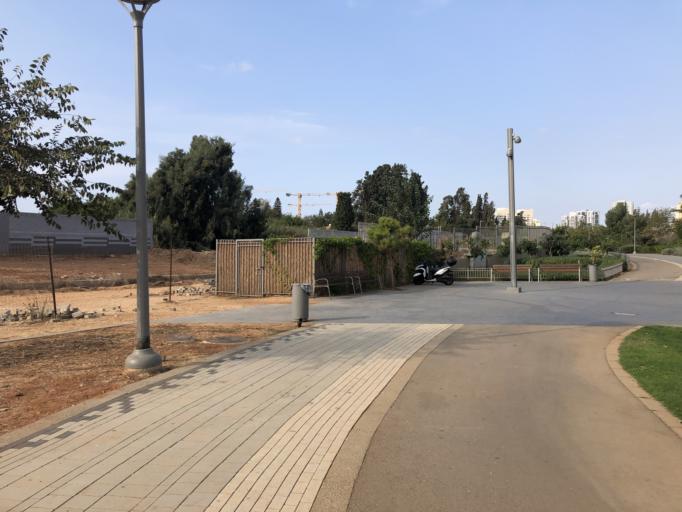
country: IL
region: Tel Aviv
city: Giv`at Shemu'el
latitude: 32.0573
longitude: 34.8450
